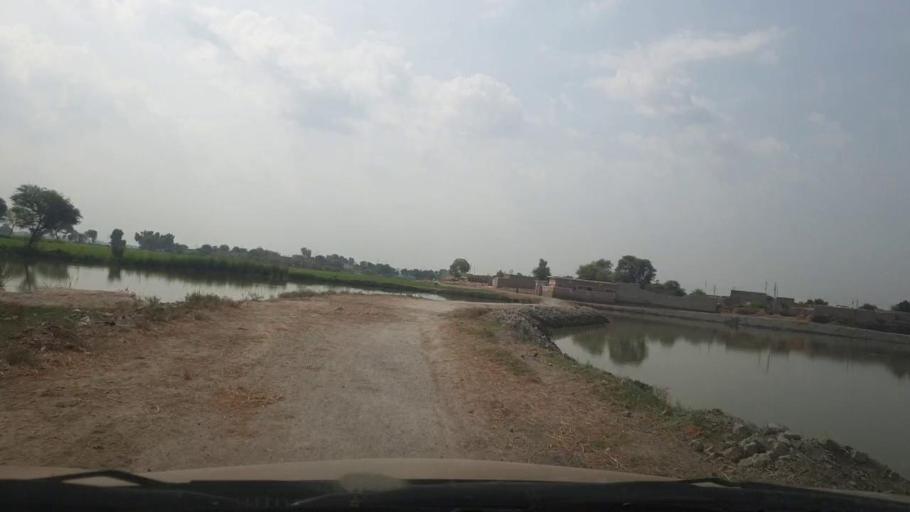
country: PK
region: Sindh
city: Larkana
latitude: 27.6505
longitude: 68.2100
